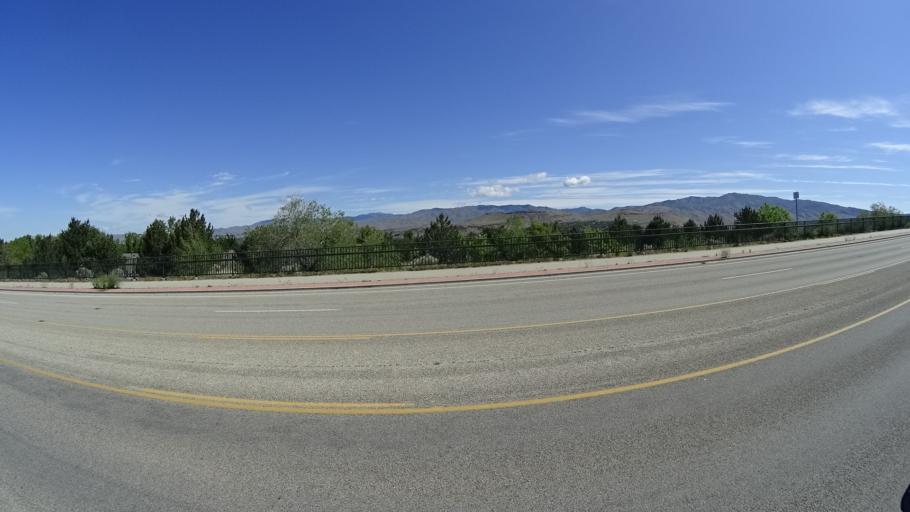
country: US
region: Idaho
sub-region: Ada County
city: Boise
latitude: 43.5648
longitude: -116.1767
